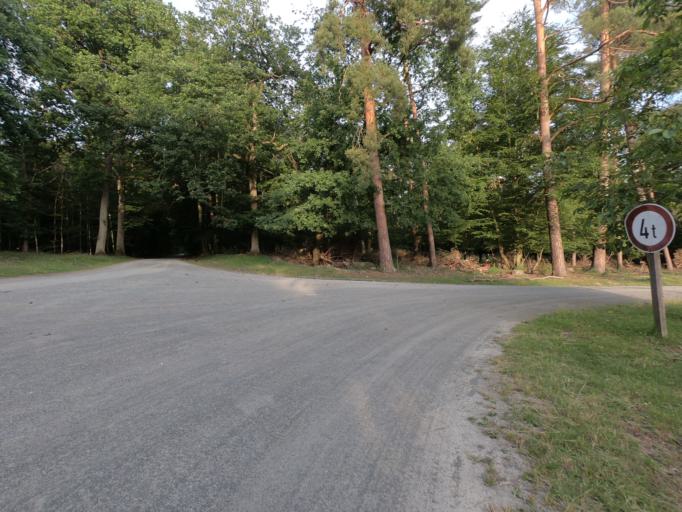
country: DE
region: Hesse
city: Raunheim
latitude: 49.9906
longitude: 8.4763
